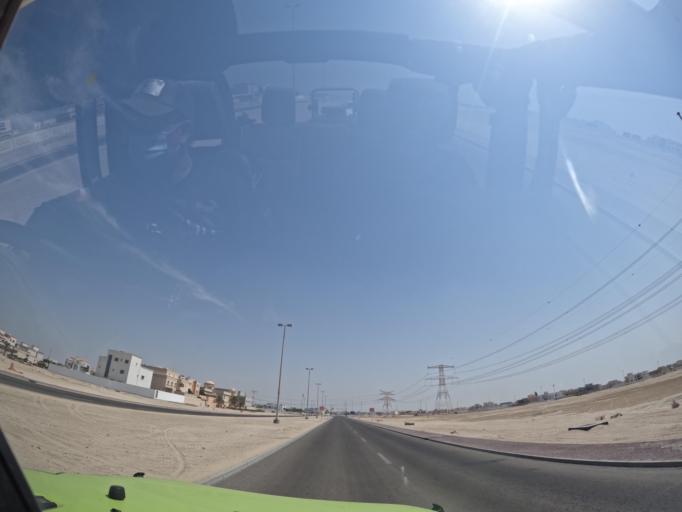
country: AE
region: Abu Dhabi
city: Abu Dhabi
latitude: 24.3076
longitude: 54.5722
